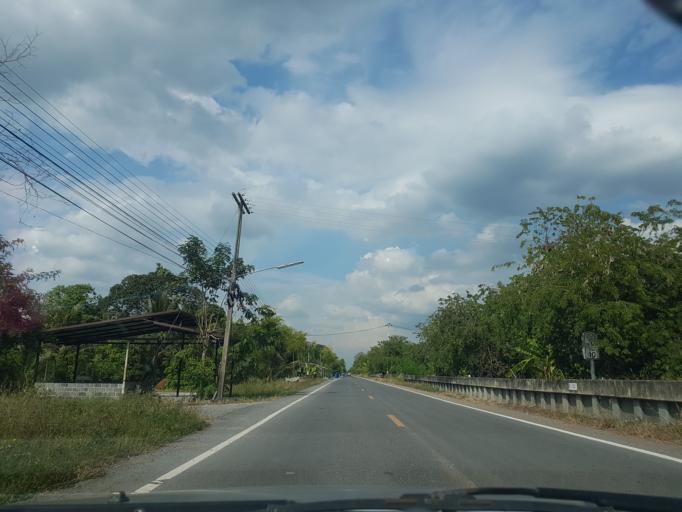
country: TH
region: Pathum Thani
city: Nong Suea
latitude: 14.1669
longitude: 100.8915
